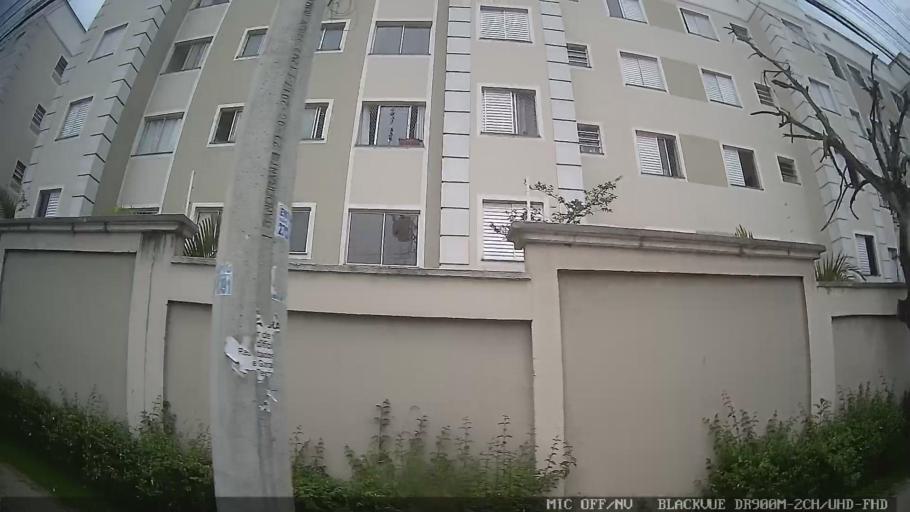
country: BR
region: Sao Paulo
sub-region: Suzano
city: Suzano
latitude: -23.5453
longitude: -46.2910
